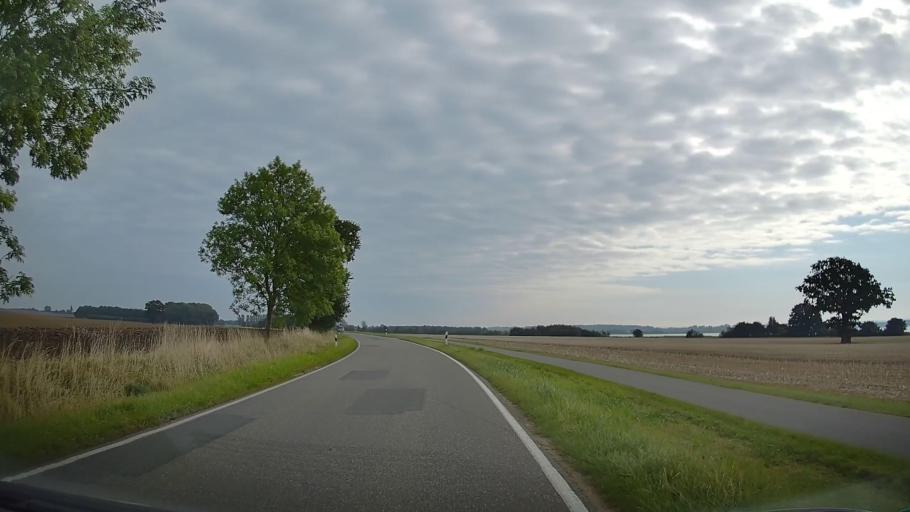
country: DE
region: Schleswig-Holstein
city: Panker
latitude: 54.3392
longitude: 10.6214
